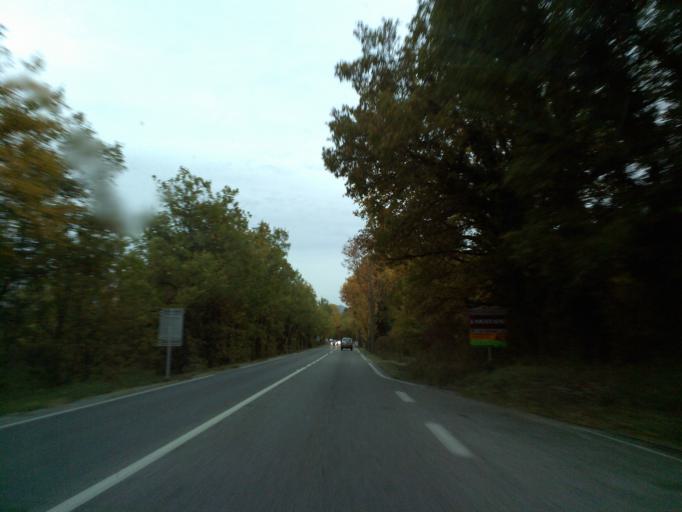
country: FR
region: Provence-Alpes-Cote d'Azur
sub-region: Departement des Alpes-de-Haute-Provence
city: Volonne
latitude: 44.1210
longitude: 5.9874
